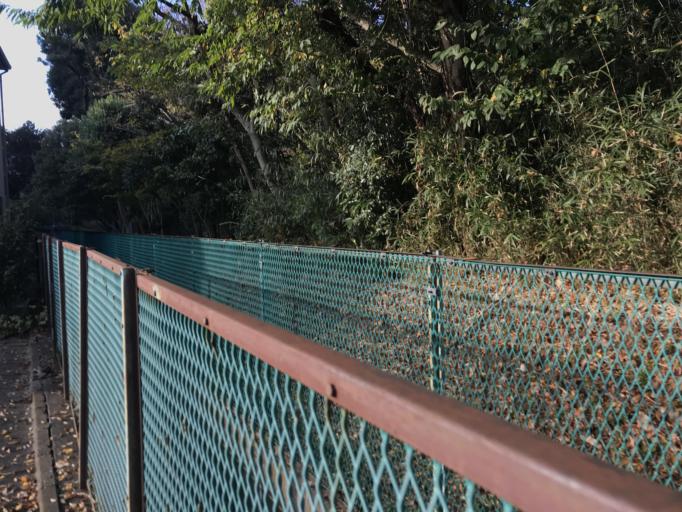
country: JP
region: Chiba
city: Funabashi
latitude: 35.7255
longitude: 139.9694
